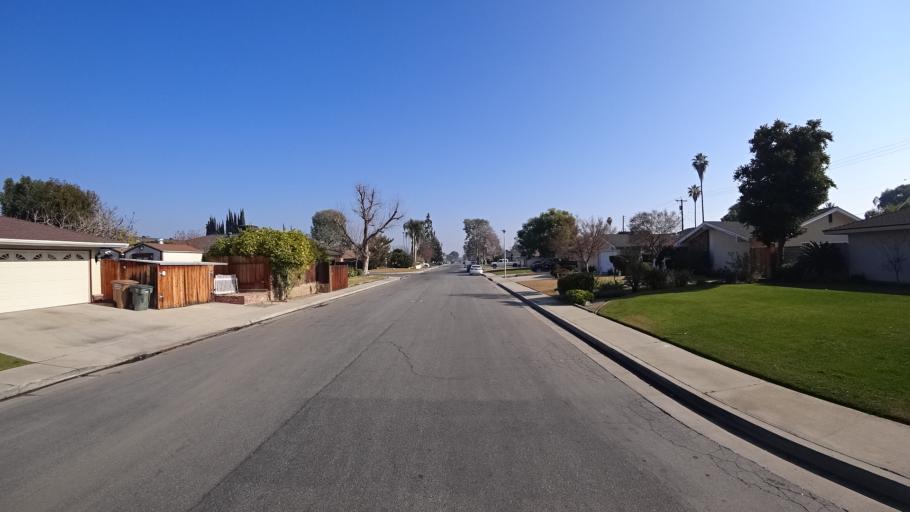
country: US
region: California
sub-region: Kern County
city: Greenacres
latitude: 35.3553
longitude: -119.0737
